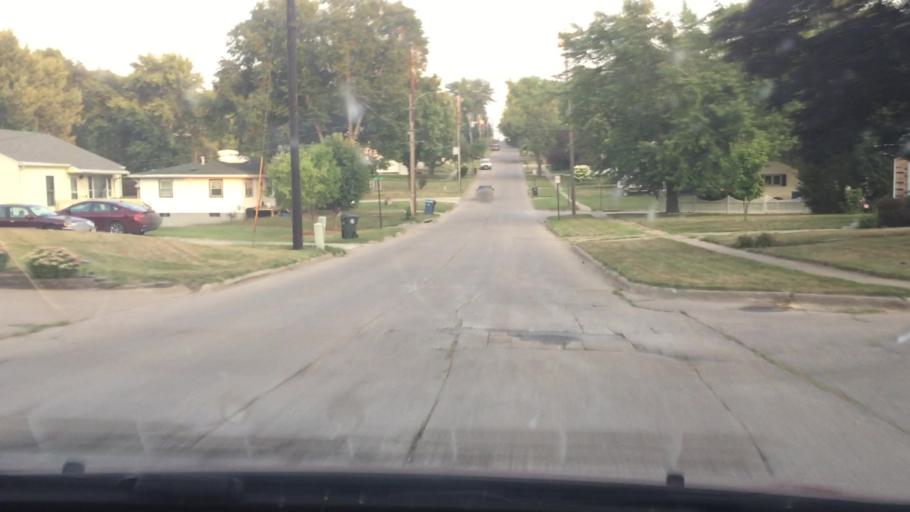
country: US
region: Iowa
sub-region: Muscatine County
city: Muscatine
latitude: 41.4280
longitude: -91.0584
